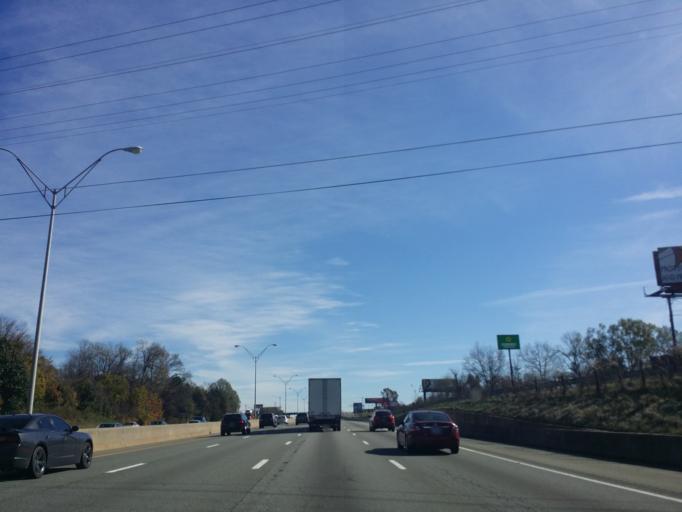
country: US
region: North Carolina
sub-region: Alamance County
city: Graham
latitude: 36.0621
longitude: -79.4130
